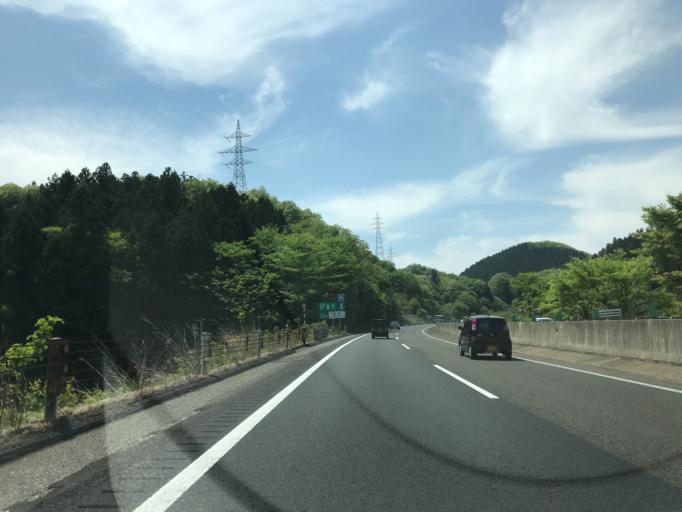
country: JP
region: Fukushima
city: Yanagawamachi-saiwaicho
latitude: 37.9161
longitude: 140.6027
